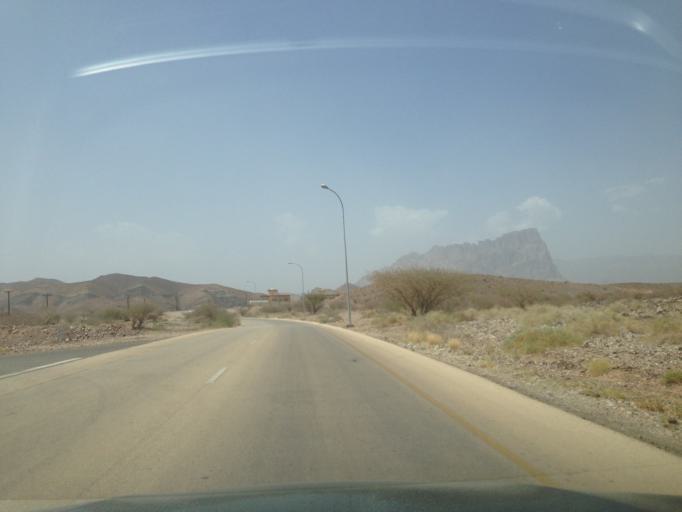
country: OM
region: Az Zahirah
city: `Ibri
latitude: 23.1800
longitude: 56.9198
